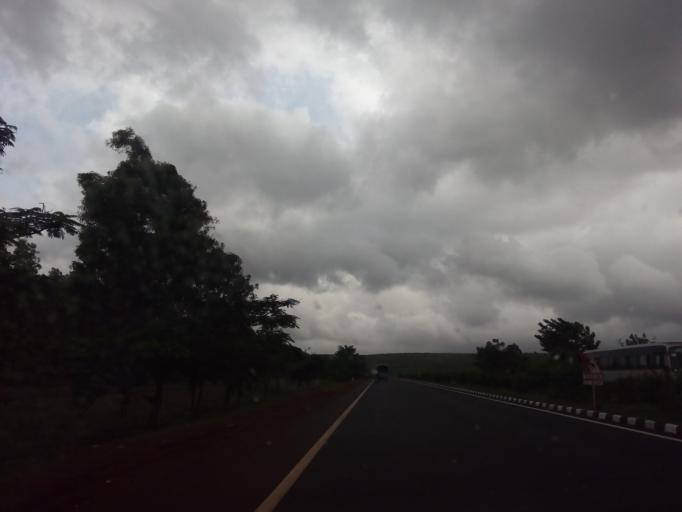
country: IN
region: Karnataka
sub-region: Belgaum
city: Hukeri
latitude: 16.0577
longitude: 74.5137
